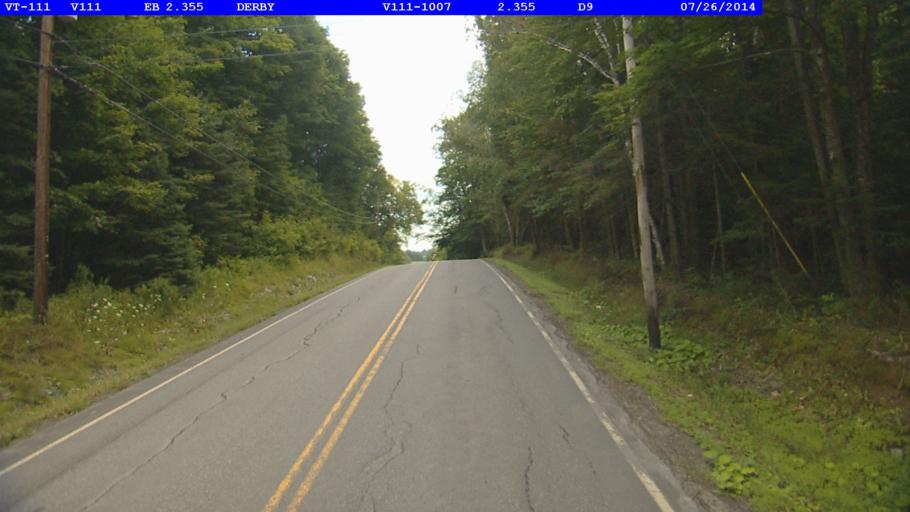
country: US
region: Vermont
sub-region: Orleans County
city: Newport
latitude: 44.9388
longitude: -72.0925
